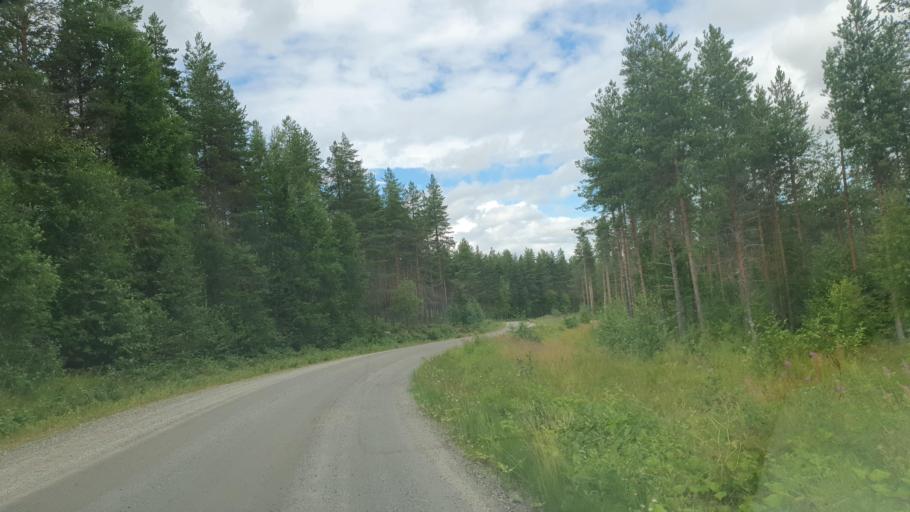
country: FI
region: Kainuu
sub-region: Kehys-Kainuu
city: Kuhmo
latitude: 64.0987
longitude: 29.4058
